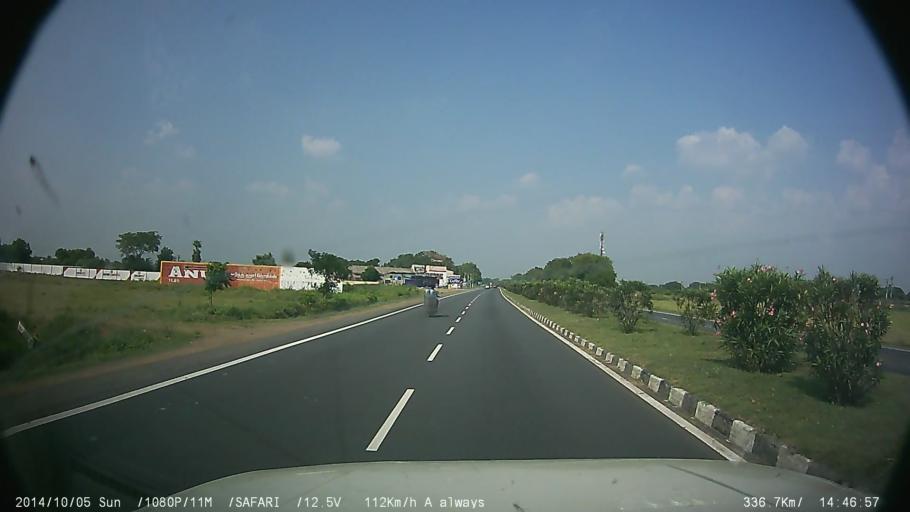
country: IN
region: Tamil Nadu
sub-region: Kancheepuram
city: Madurantakam
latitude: 12.4699
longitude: 79.8530
